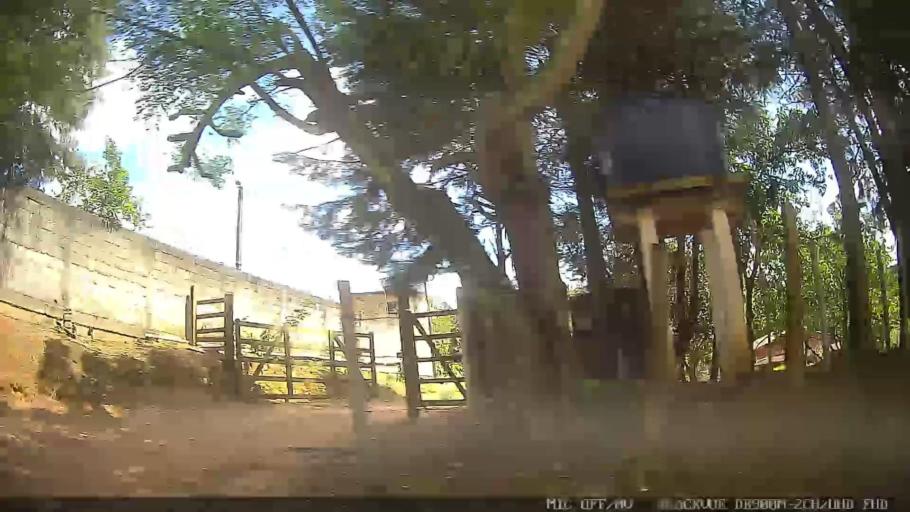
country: BR
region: Sao Paulo
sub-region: Braganca Paulista
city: Braganca Paulista
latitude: -22.8628
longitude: -46.6903
